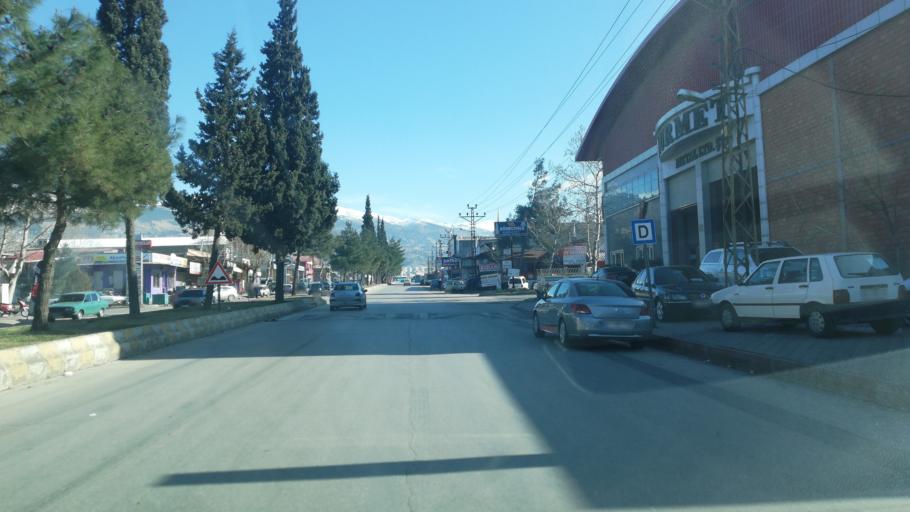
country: TR
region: Kahramanmaras
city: Kahramanmaras
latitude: 37.5642
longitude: 36.9604
